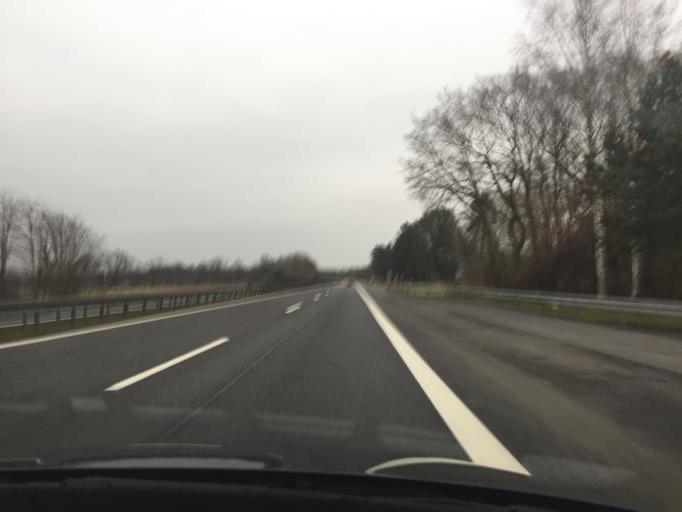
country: DE
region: Brandenburg
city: Lubbenau
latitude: 51.8436
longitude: 13.9261
